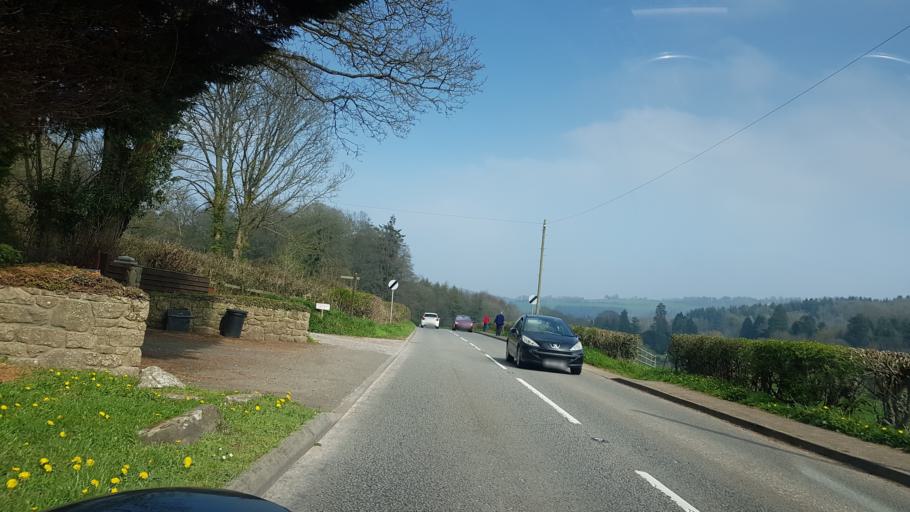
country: GB
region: Wales
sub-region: Monmouthshire
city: Tintern
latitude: 51.7367
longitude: -2.6774
